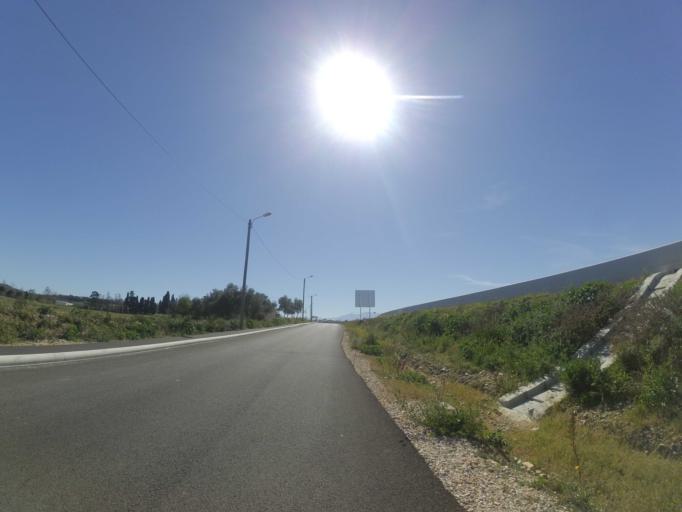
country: FR
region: Languedoc-Roussillon
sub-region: Departement des Pyrenees-Orientales
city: Saint-Esteve
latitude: 42.6816
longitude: 2.8635
